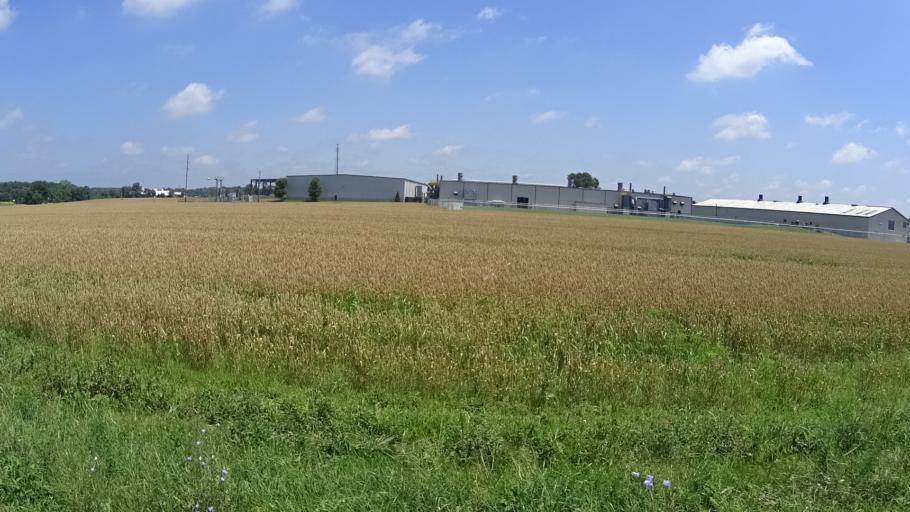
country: US
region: Ohio
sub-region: Huron County
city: Wakeman
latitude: 41.3305
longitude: -82.3738
